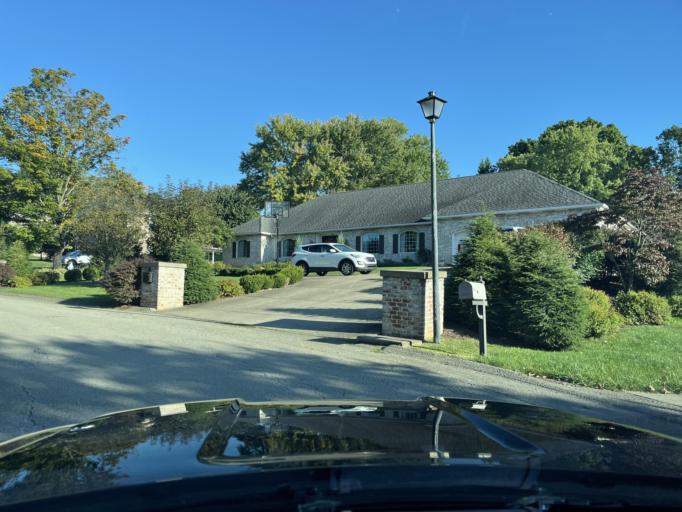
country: US
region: Pennsylvania
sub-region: Fayette County
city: Leith-Hatfield
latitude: 39.8764
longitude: -79.7333
